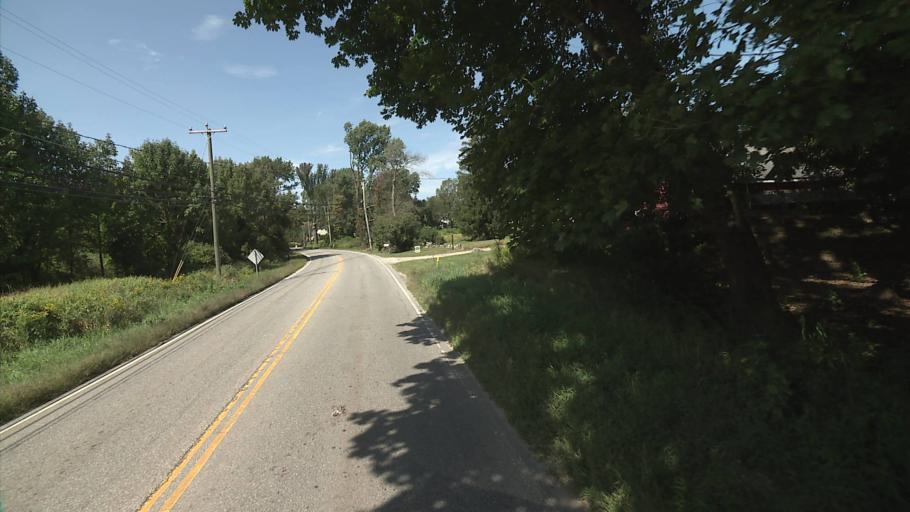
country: US
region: Connecticut
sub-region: Windham County
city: South Windham
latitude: 41.6279
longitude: -72.1995
